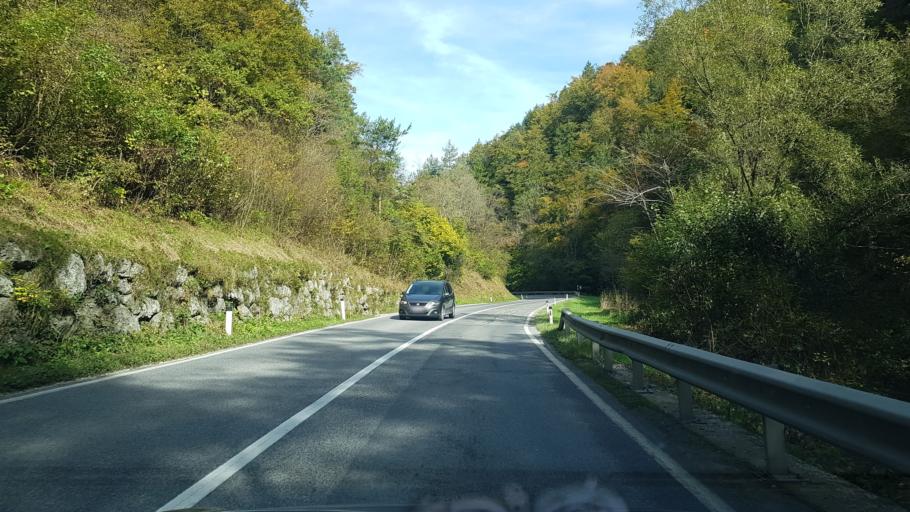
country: SI
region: Velenje
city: Velenje
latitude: 46.3890
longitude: 15.1644
